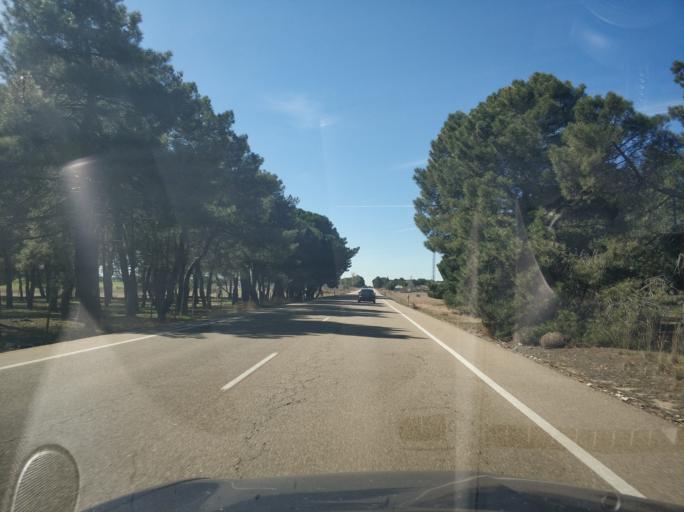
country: ES
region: Castille and Leon
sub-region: Provincia de Valladolid
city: Boecillo
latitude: 41.5424
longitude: -4.6815
